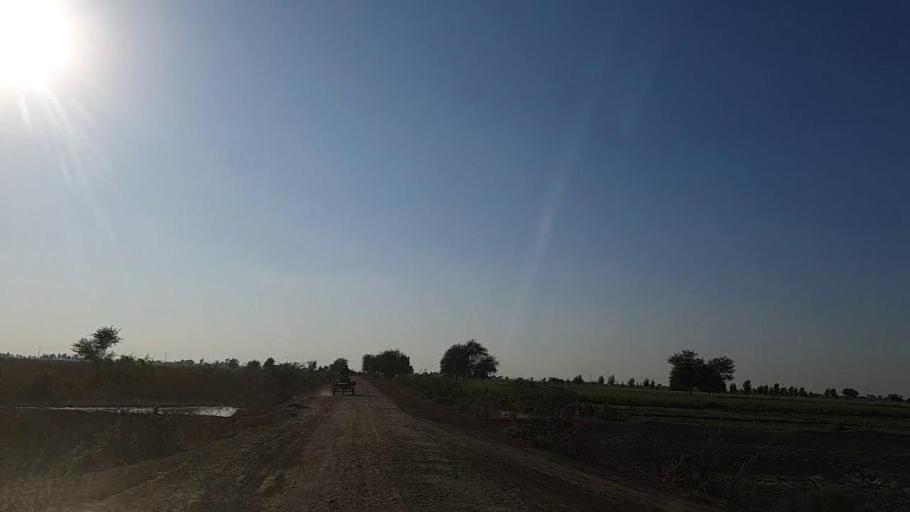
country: PK
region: Sindh
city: Samaro
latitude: 25.3442
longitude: 69.3797
